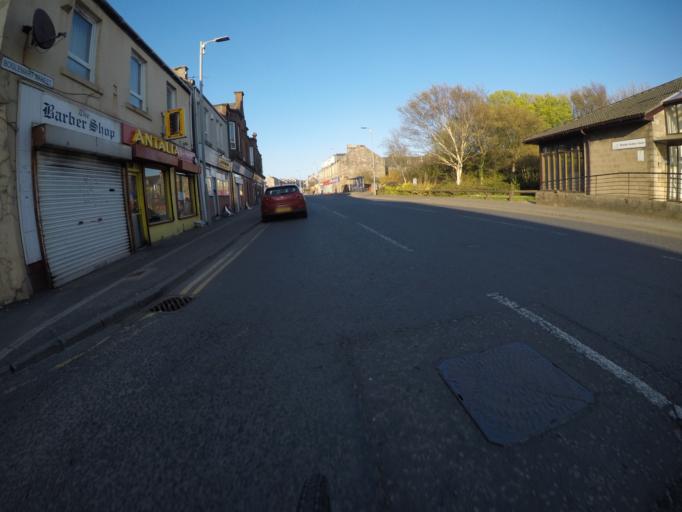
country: GB
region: Scotland
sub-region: North Ayrshire
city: Stevenston
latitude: 55.6403
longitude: -4.7585
